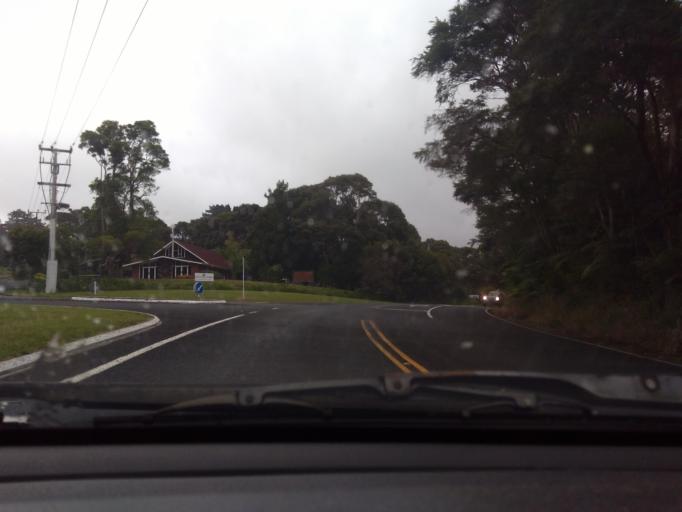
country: NZ
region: Auckland
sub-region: Auckland
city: Waitakere
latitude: -36.9191
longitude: 174.6124
